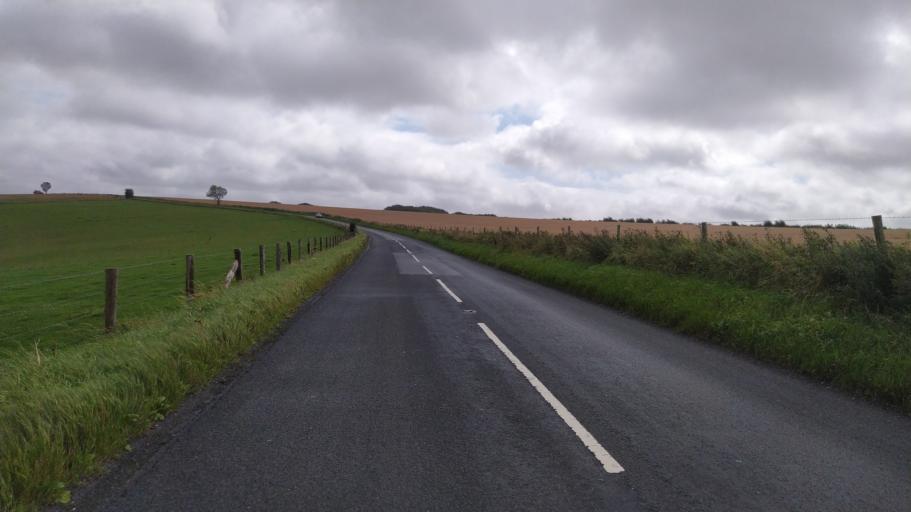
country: GB
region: England
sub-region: Dorset
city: Shaftesbury
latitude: 50.9809
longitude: -2.1317
